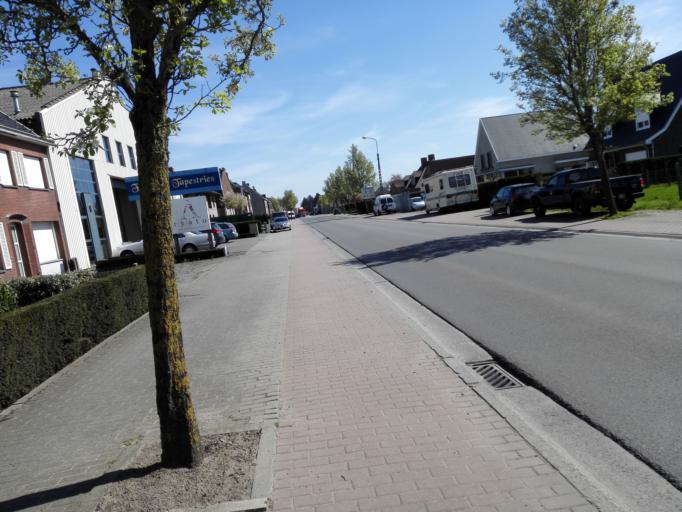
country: BE
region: Flanders
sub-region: Provincie West-Vlaanderen
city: Wielsbeke
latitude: 50.9148
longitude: 3.3662
